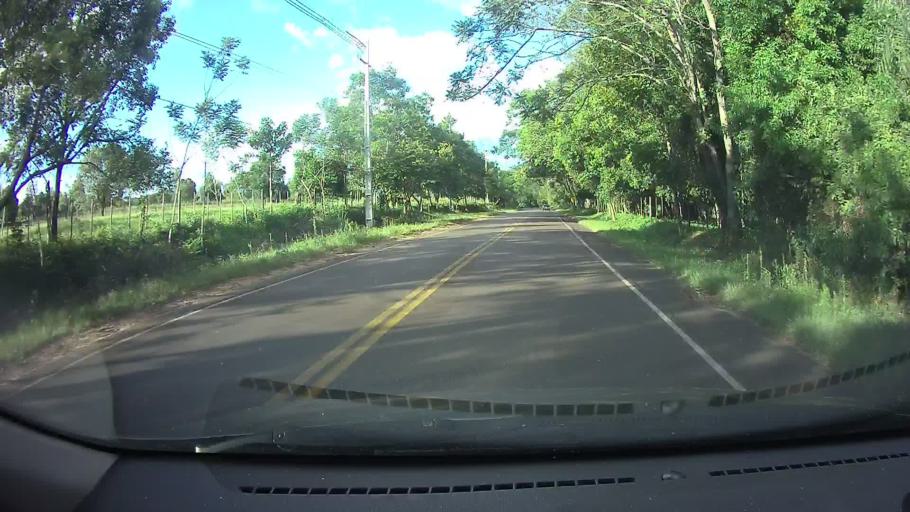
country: PY
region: Cordillera
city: Altos
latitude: -25.2287
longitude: -57.2279
